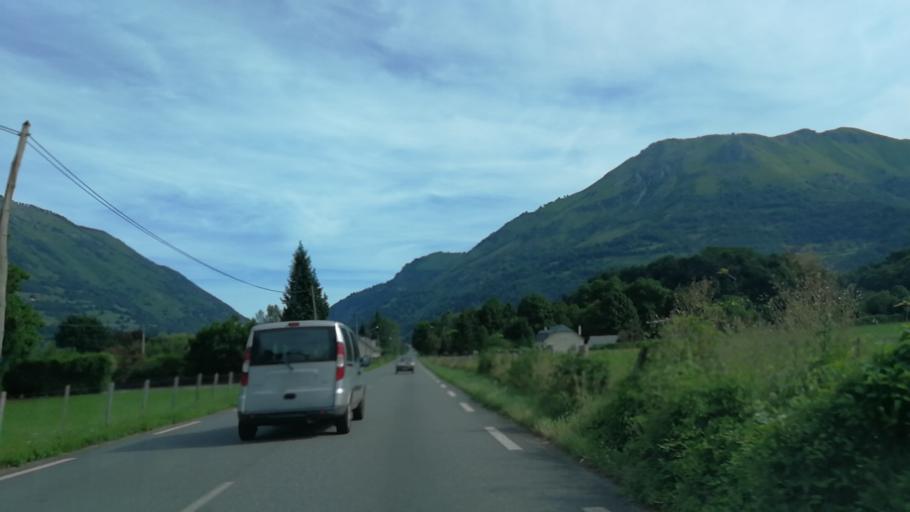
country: FR
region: Aquitaine
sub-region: Departement des Pyrenees-Atlantiques
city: Arette
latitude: 42.9824
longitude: -0.6058
